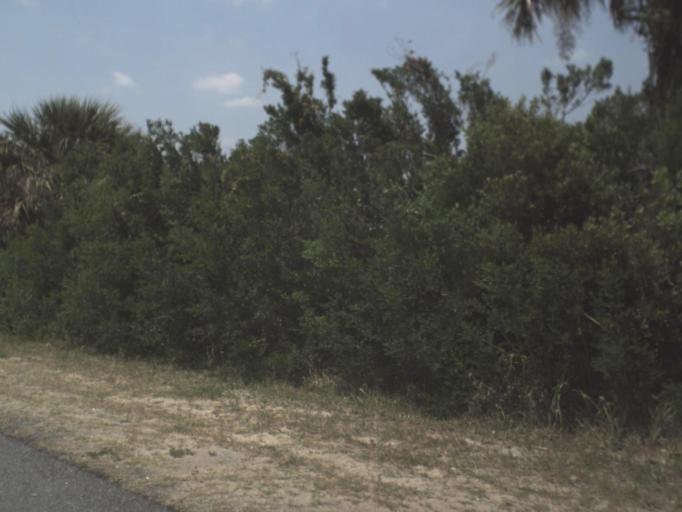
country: US
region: Florida
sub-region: Duval County
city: Atlantic Beach
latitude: 30.3780
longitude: -81.4373
